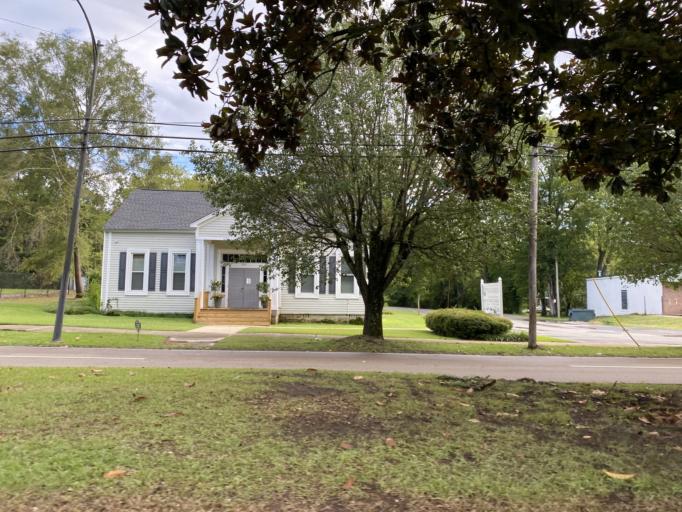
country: US
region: Mississippi
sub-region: Monroe County
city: Aberdeen
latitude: 33.8255
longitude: -88.5498
